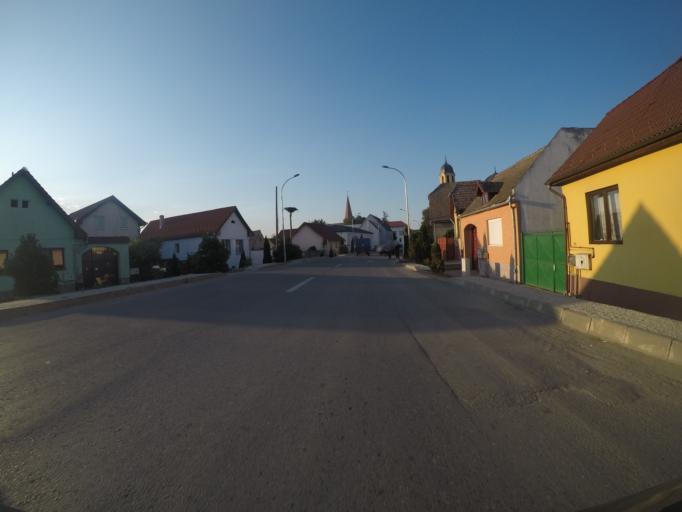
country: RO
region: Sibiu
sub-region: Comuna Selimbar
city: Selimbar
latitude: 45.7660
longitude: 24.1959
